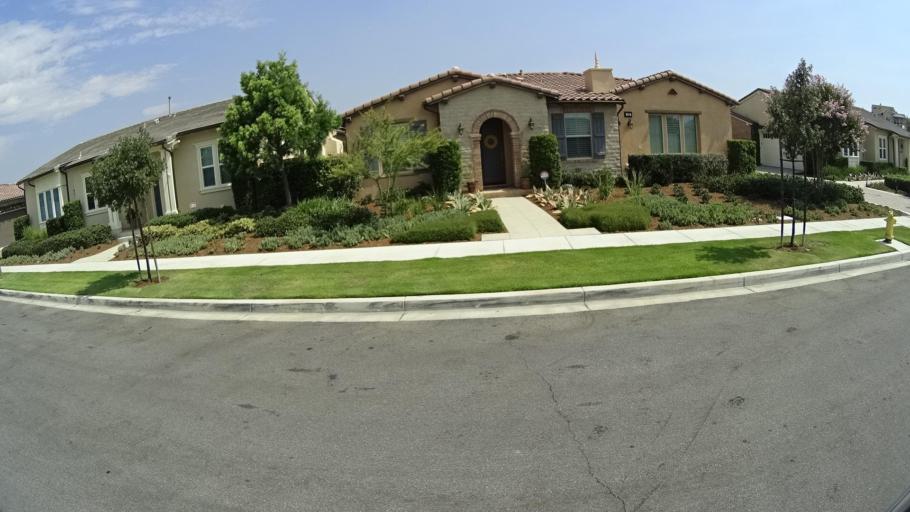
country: US
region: California
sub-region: Orange County
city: Ladera Ranch
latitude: 33.5428
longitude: -117.6020
